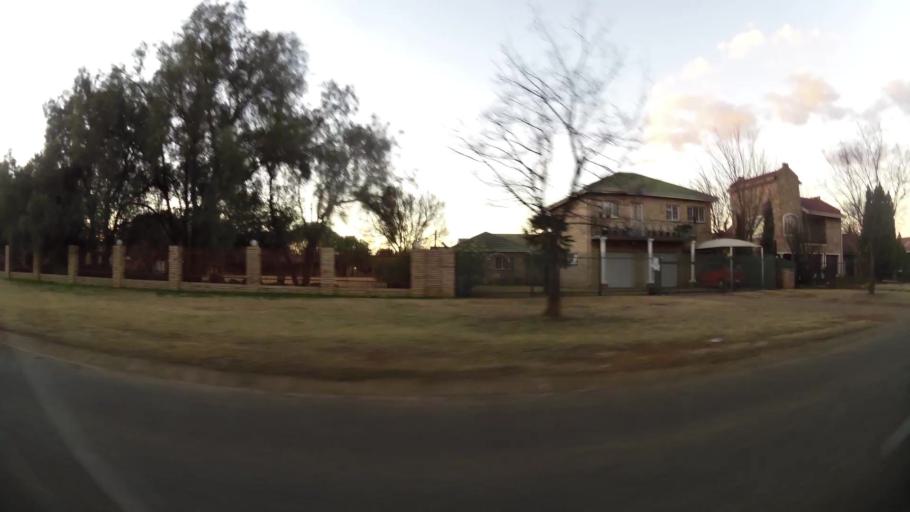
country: ZA
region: North-West
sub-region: Dr Kenneth Kaunda District Municipality
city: Potchefstroom
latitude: -26.7140
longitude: 27.1200
